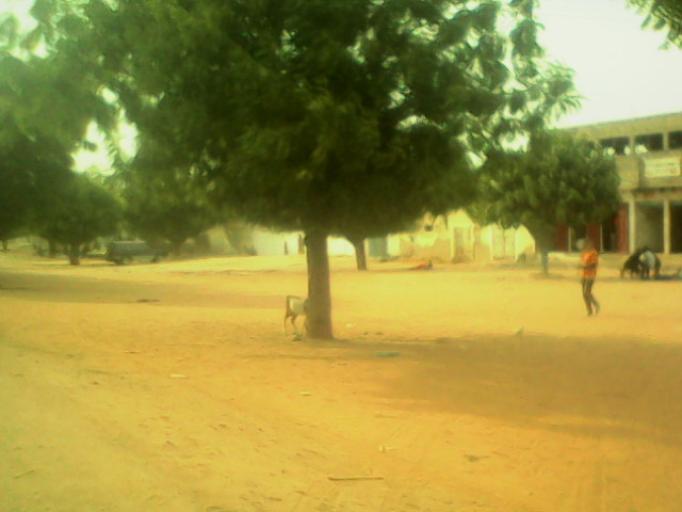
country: SN
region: Diourbel
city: Touba
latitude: 14.8847
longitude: -15.8777
